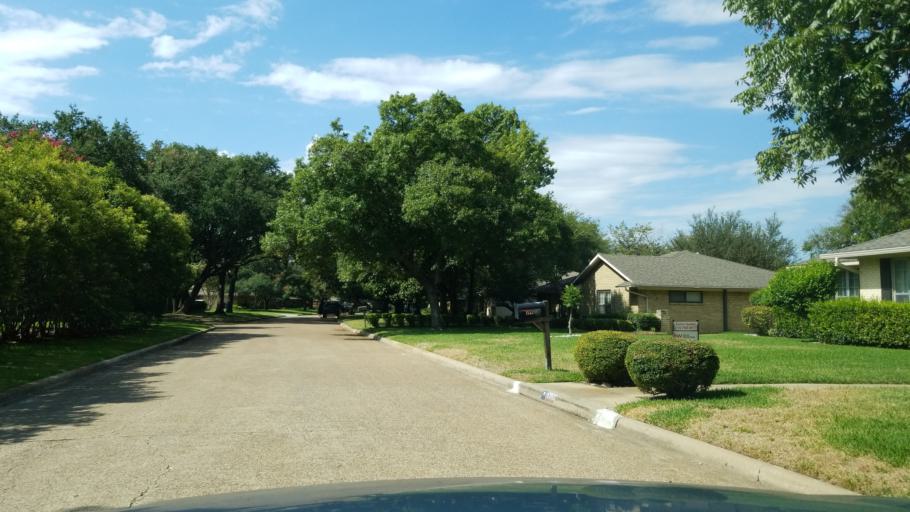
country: US
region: Texas
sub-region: Dallas County
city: Richardson
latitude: 32.9558
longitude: -96.7707
